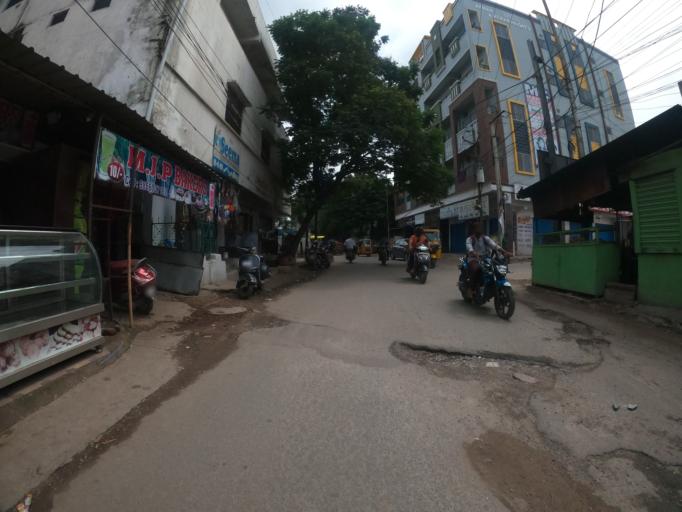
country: IN
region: Telangana
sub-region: Hyderabad
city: Hyderabad
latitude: 17.3931
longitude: 78.4174
